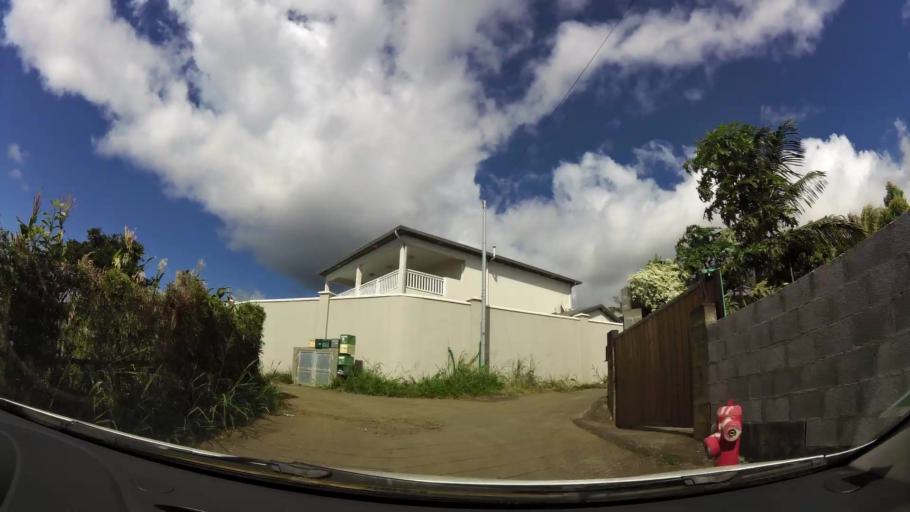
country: RE
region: Reunion
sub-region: Reunion
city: Sainte-Marie
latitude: -20.9278
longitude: 55.4999
